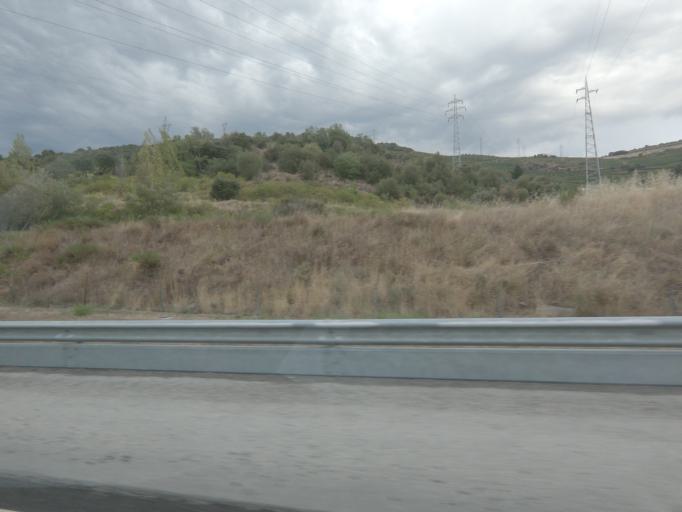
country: PT
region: Vila Real
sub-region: Peso da Regua
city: Peso da Regua
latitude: 41.1402
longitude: -7.7722
